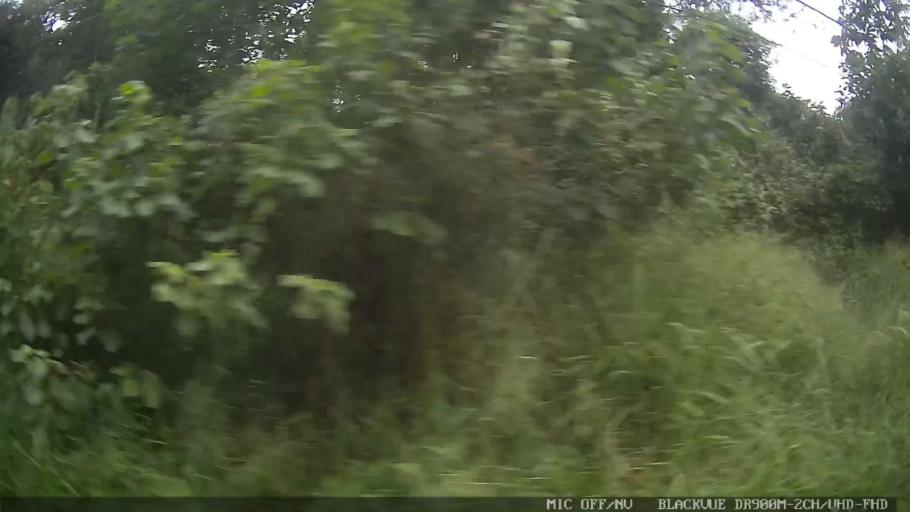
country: BR
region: Sao Paulo
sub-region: Mogi das Cruzes
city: Mogi das Cruzes
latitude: -23.5412
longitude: -46.1172
